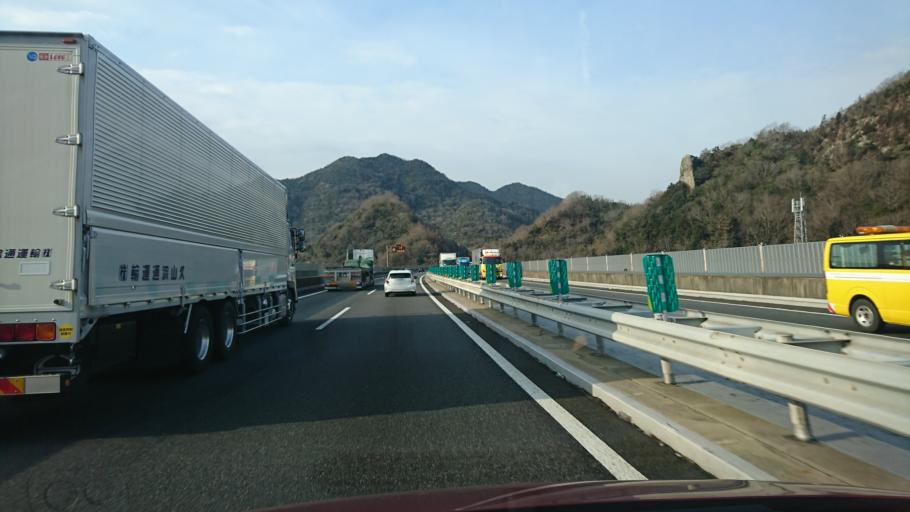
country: JP
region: Hyogo
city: Kariya
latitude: 34.7890
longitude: 134.1676
